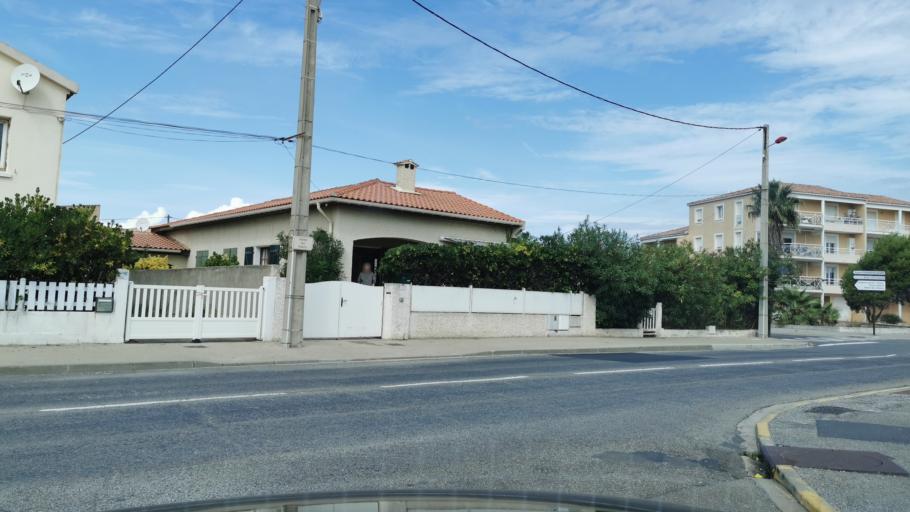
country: FR
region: Languedoc-Roussillon
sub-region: Departement de l'Aude
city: Fleury
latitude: 43.1615
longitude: 3.1678
